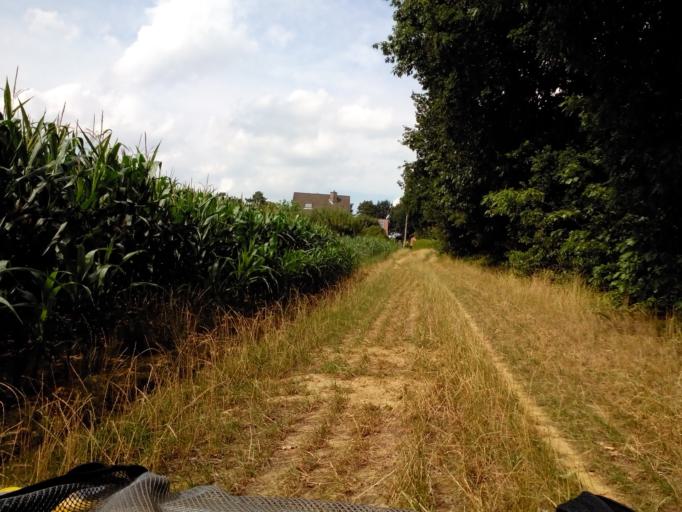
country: BE
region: Flanders
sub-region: Provincie Vlaams-Brabant
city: Holsbeek
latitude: 50.8969
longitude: 4.7888
